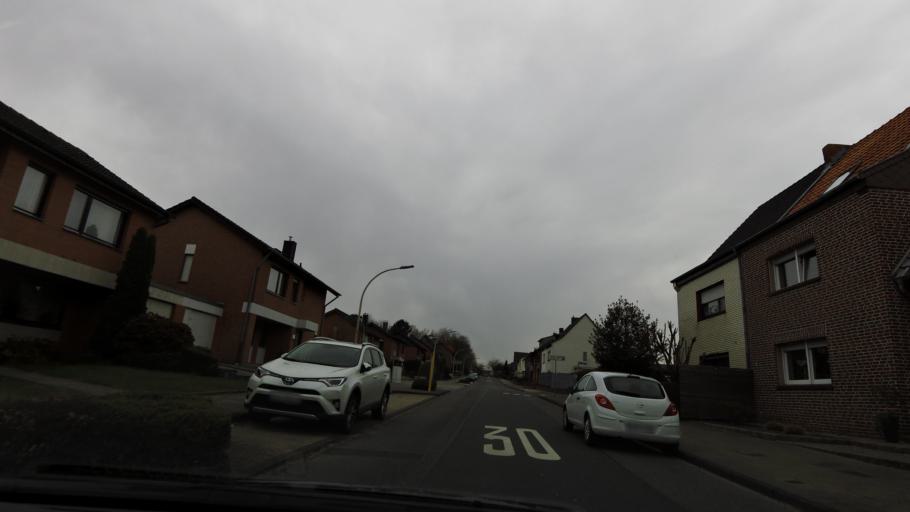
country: DE
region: North Rhine-Westphalia
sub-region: Regierungsbezirk Koln
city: Ubach-Palenberg
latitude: 50.9186
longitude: 6.1125
